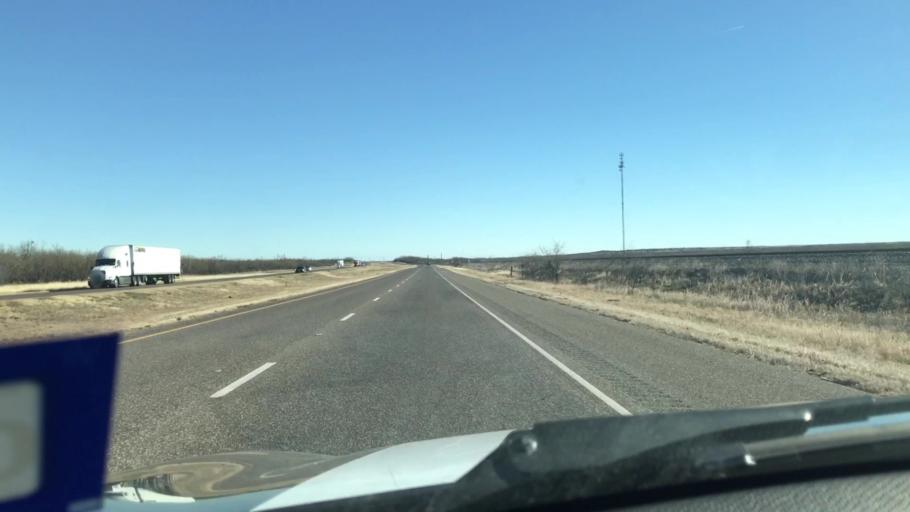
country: US
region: Texas
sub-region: Scurry County
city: Snyder
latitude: 32.8626
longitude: -101.0277
